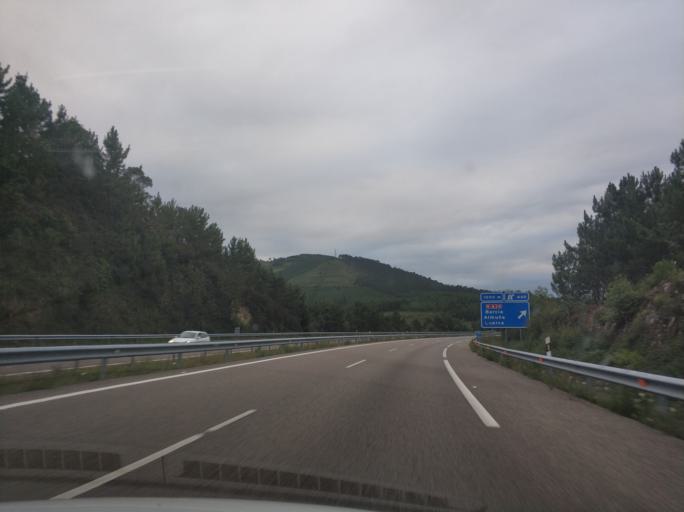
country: ES
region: Asturias
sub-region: Province of Asturias
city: Tineo
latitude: 43.5351
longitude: -6.4850
